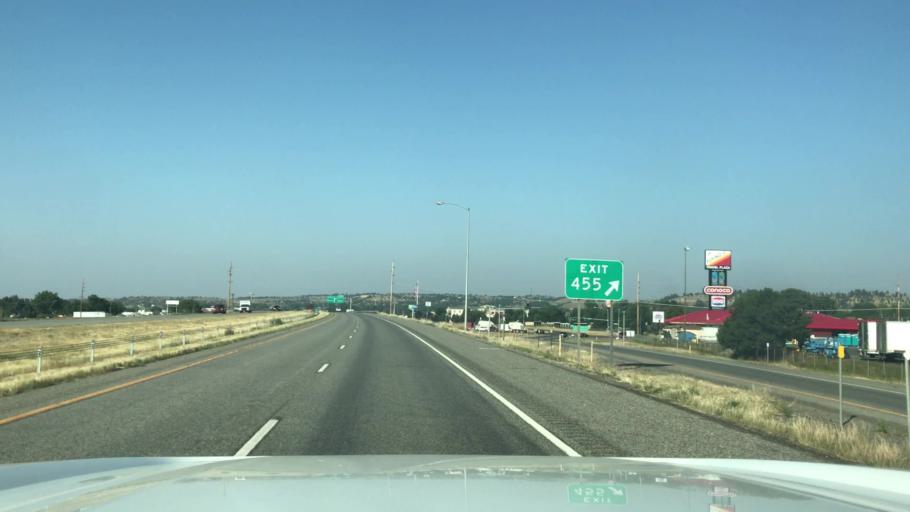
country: US
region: Montana
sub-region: Yellowstone County
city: Lockwood
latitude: 45.8125
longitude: -108.4179
